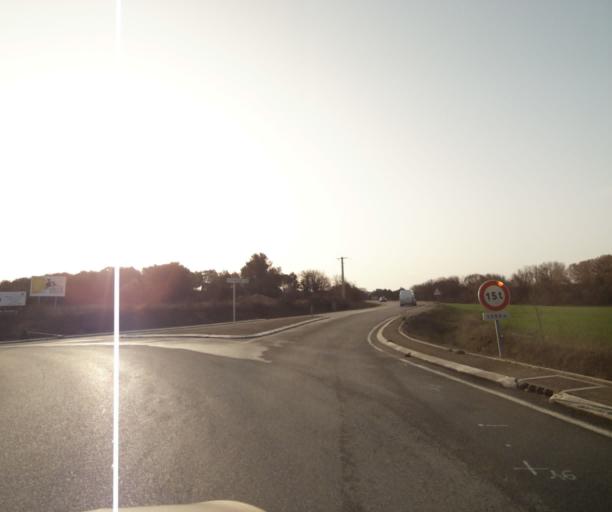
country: FR
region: Provence-Alpes-Cote d'Azur
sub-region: Departement des Bouches-du-Rhone
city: Peynier
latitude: 43.4609
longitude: 5.6281
